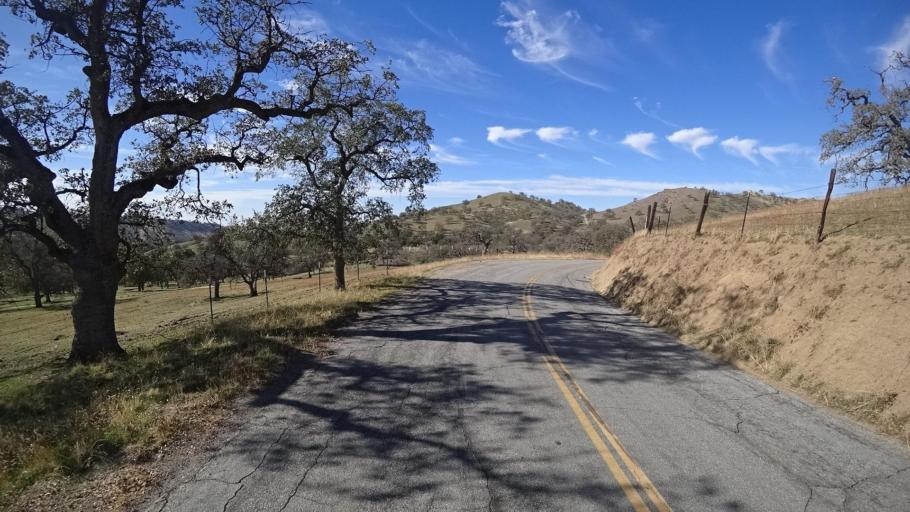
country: US
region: California
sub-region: Kern County
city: Alta Sierra
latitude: 35.6297
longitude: -118.7974
